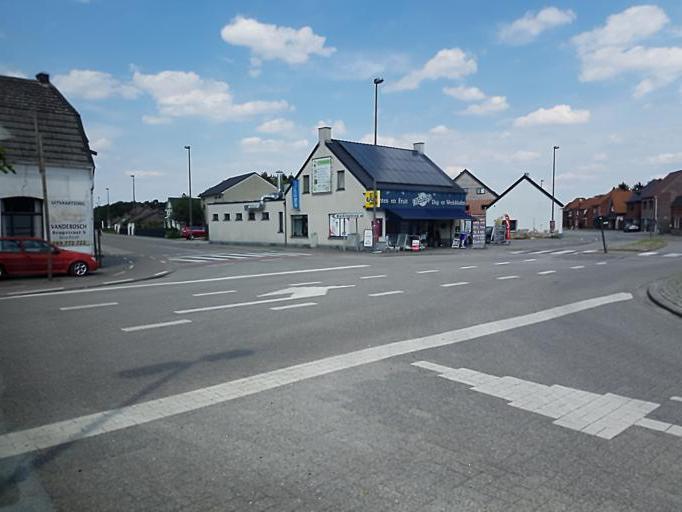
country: BE
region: Flanders
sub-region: Provincie Limburg
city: Bocholt
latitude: 51.1916
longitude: 5.5156
